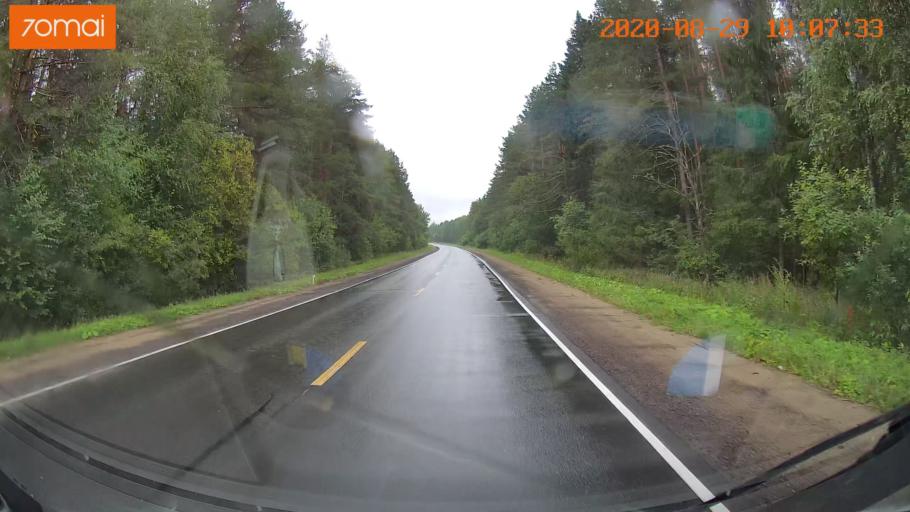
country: RU
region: Ivanovo
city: Kuznechikha
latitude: 57.3800
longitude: 42.5692
